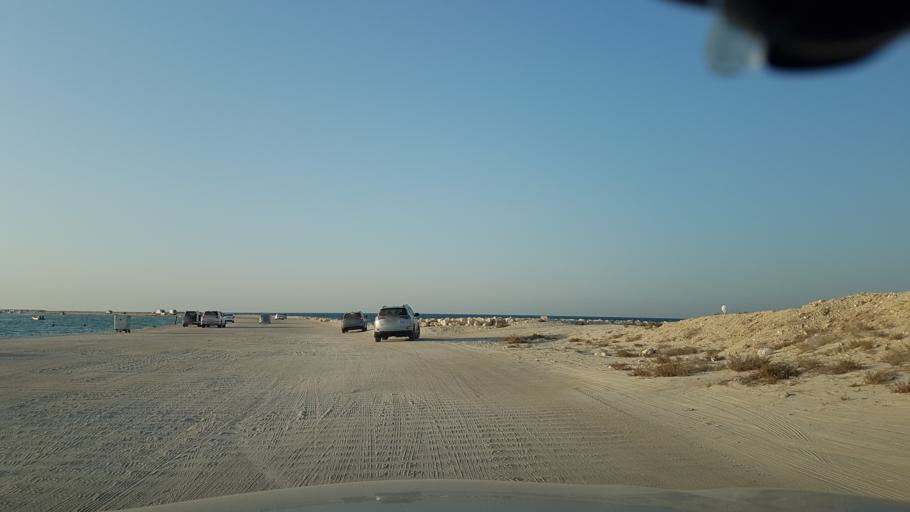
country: BH
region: Manama
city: Jidd Hafs
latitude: 26.2475
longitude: 50.5027
